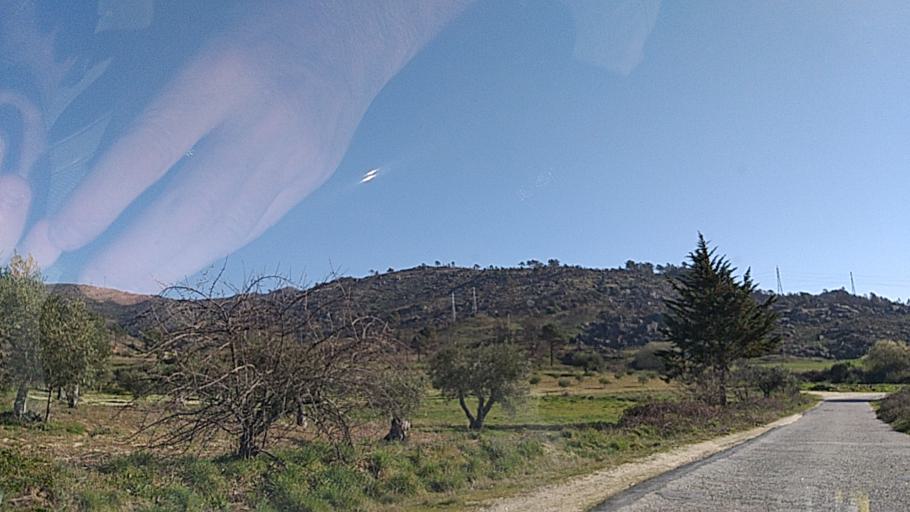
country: PT
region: Guarda
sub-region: Celorico da Beira
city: Celorico da Beira
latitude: 40.6908
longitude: -7.4230
